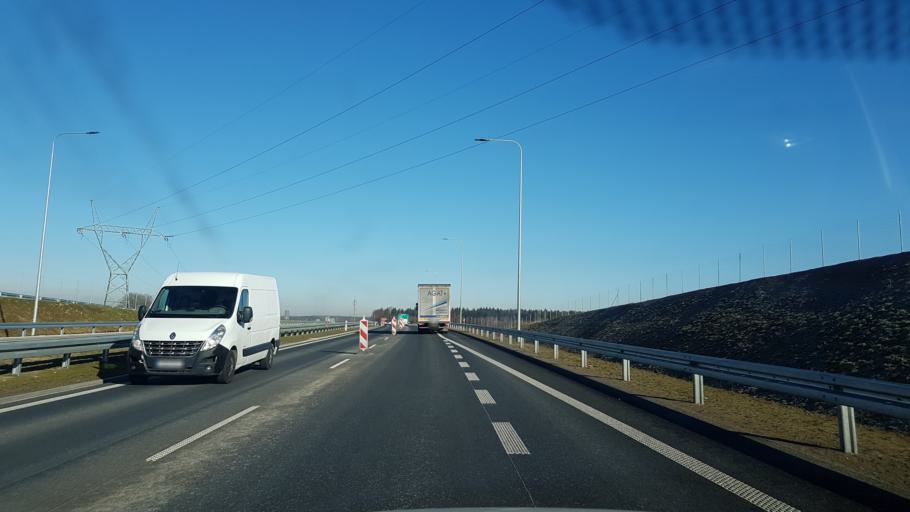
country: PL
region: West Pomeranian Voivodeship
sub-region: Powiat goleniowski
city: Przybiernow
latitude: 53.7932
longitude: 14.7776
